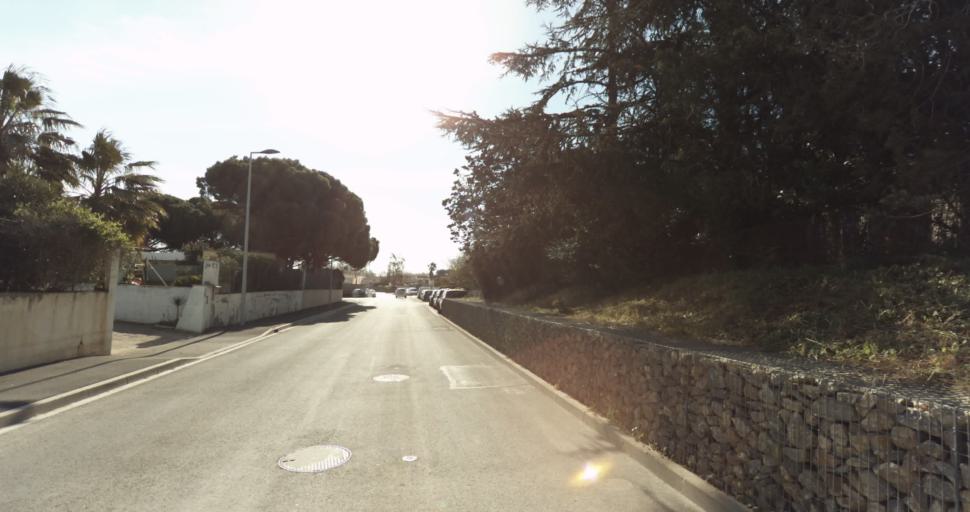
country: FR
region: Languedoc-Roussillon
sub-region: Departement de l'Herault
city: Marseillan
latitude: 43.3581
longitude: 3.5198
